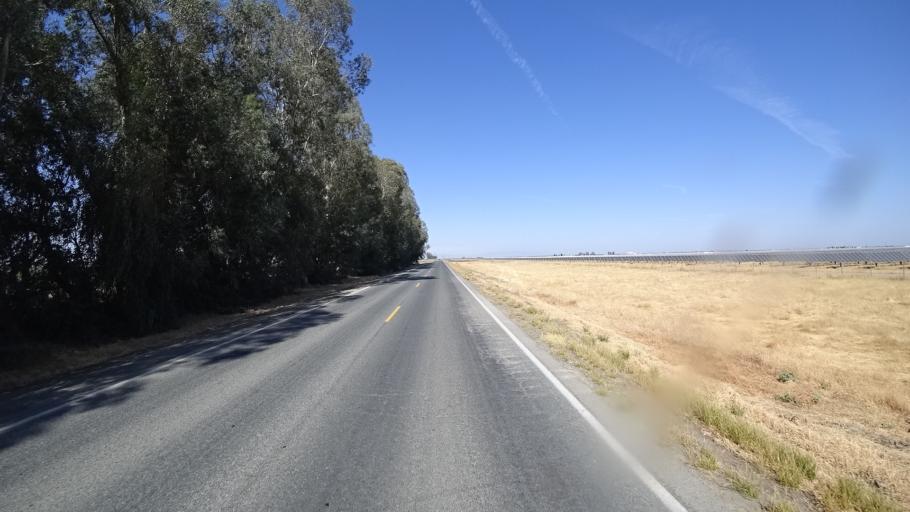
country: US
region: California
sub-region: Kings County
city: Stratford
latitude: 36.2114
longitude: -119.8051
